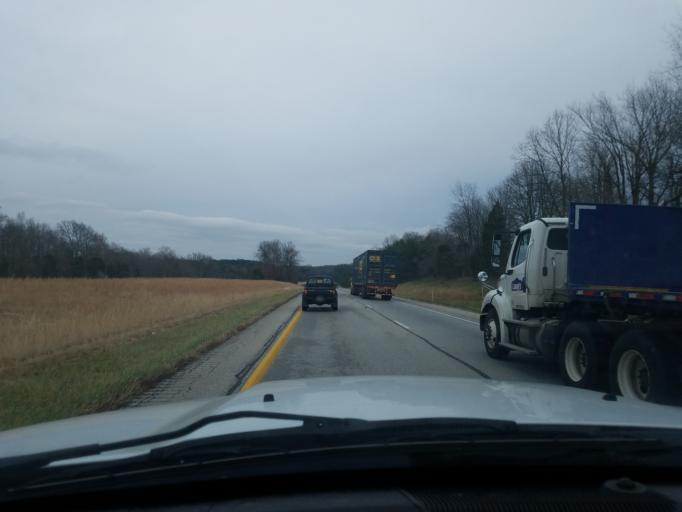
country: US
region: Indiana
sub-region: Floyd County
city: Georgetown
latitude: 38.2524
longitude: -86.0410
